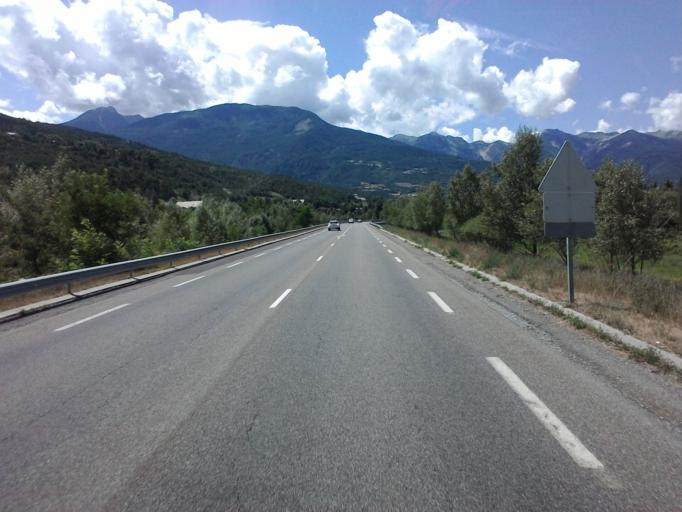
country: FR
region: Provence-Alpes-Cote d'Azur
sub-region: Departement des Hautes-Alpes
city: Embrun
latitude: 44.5604
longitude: 6.5063
